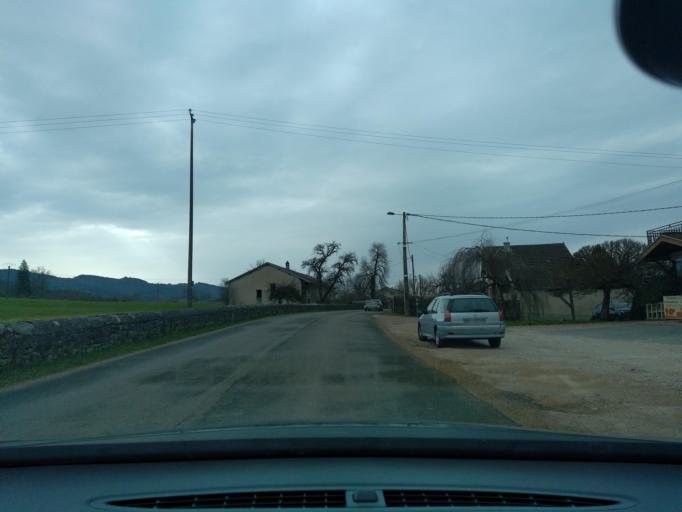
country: FR
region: Franche-Comte
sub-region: Departement du Jura
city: Arinthod
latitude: 46.3817
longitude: 5.5644
